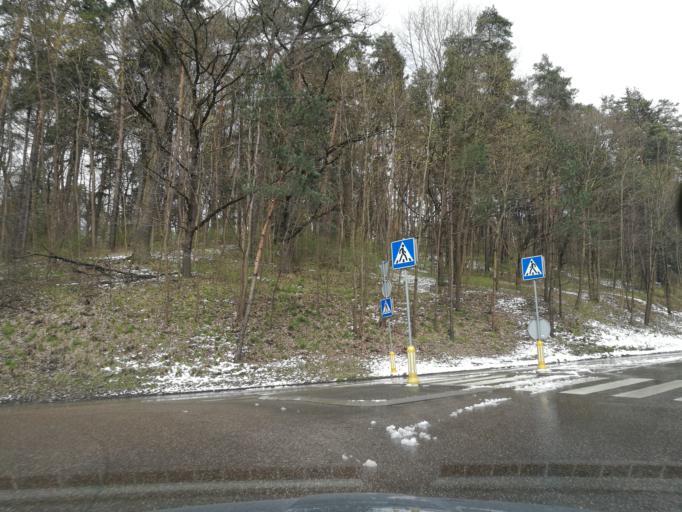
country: LT
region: Kauno apskritis
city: Dainava (Kaunas)
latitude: 54.8702
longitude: 23.9816
